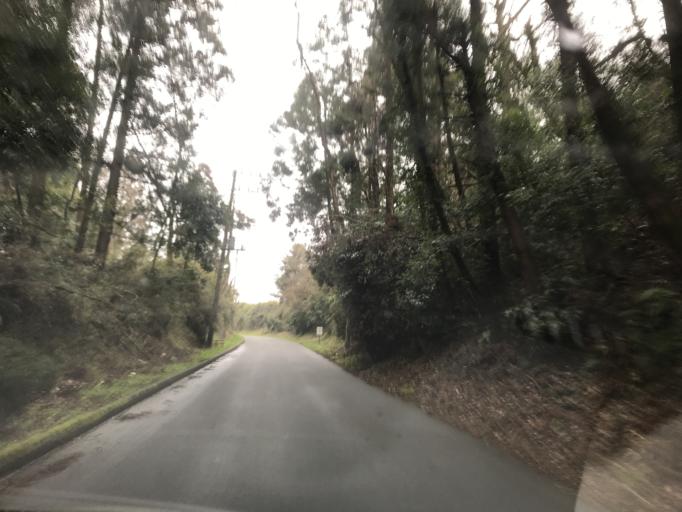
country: JP
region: Chiba
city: Sawara
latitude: 35.8506
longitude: 140.5375
